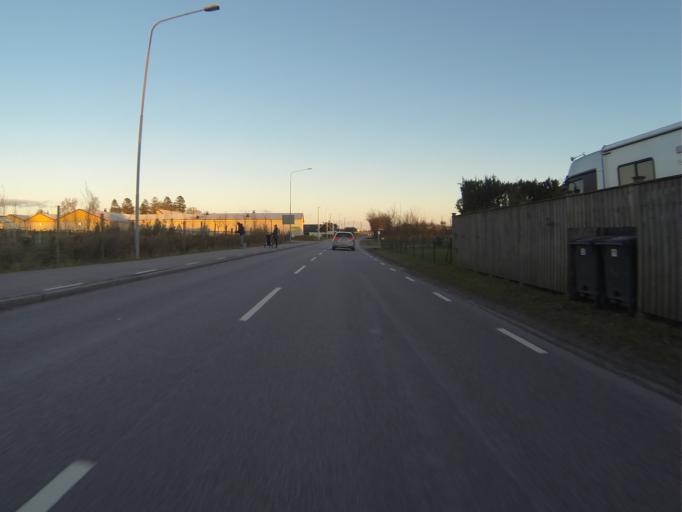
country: SE
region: Skane
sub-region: Eslovs Kommun
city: Eslov
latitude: 55.7514
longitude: 13.3744
